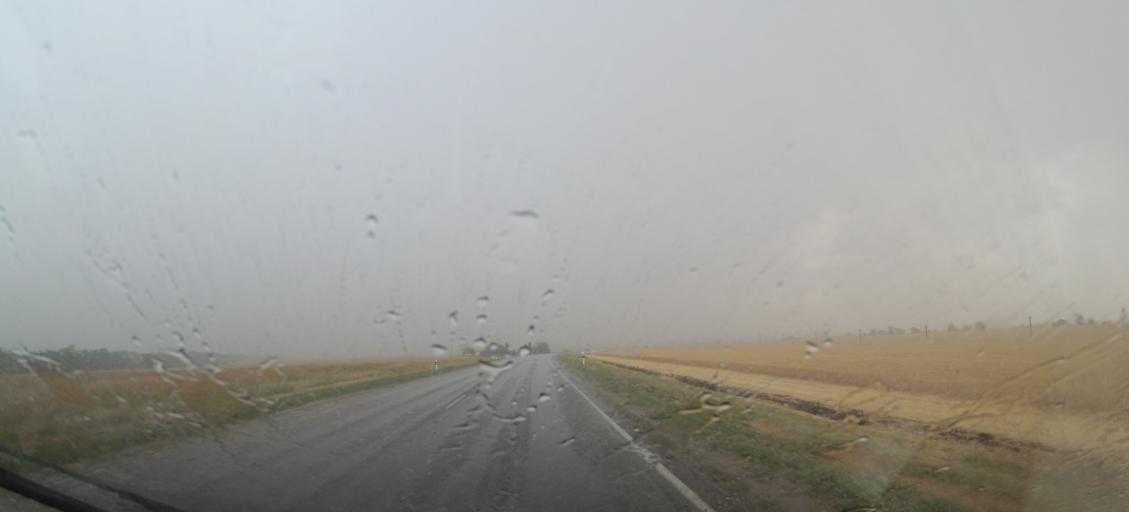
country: RU
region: Rostov
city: Proletarsk
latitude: 46.6741
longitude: 41.6974
